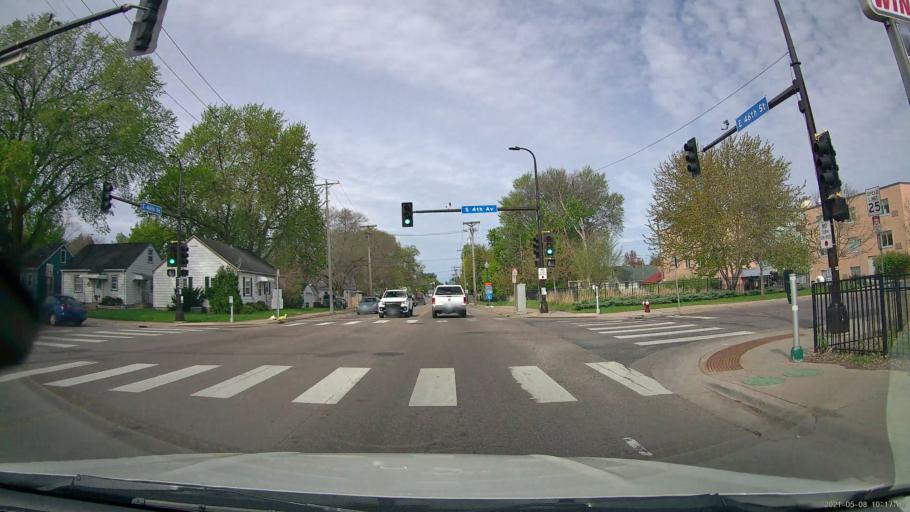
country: US
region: Minnesota
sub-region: Hennepin County
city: Richfield
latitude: 44.9197
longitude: -93.2702
